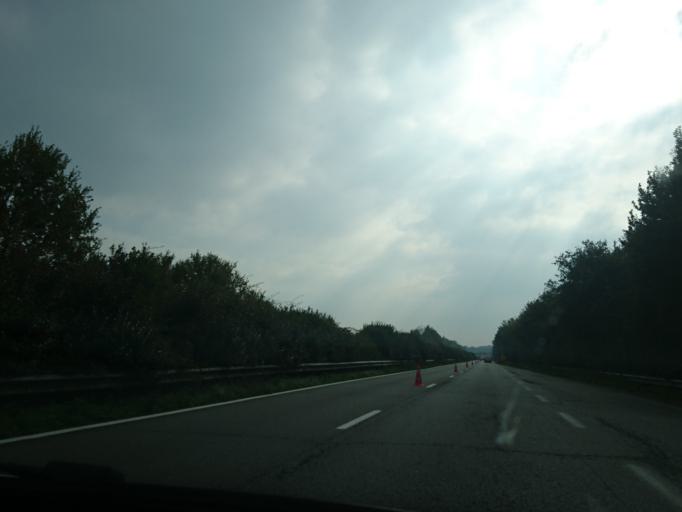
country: FR
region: Pays de la Loire
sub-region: Departement de la Loire-Atlantique
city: Nozay
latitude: 47.5743
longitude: -1.6311
